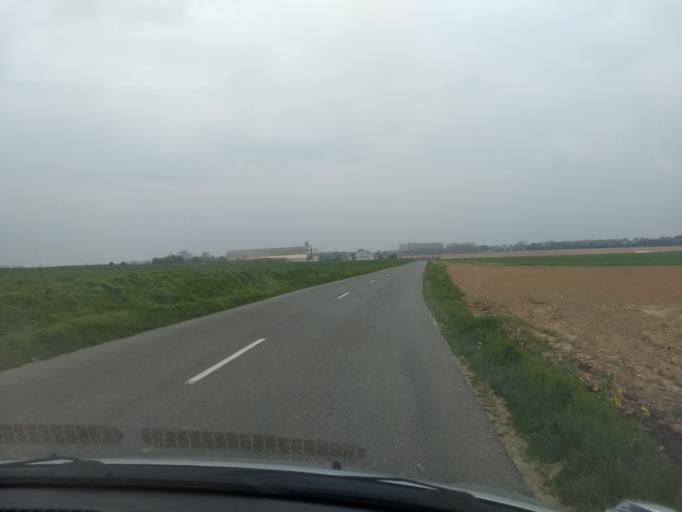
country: FR
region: Nord-Pas-de-Calais
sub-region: Departement du Pas-de-Calais
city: Neuville-Saint-Vaast
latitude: 50.3515
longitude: 2.7305
